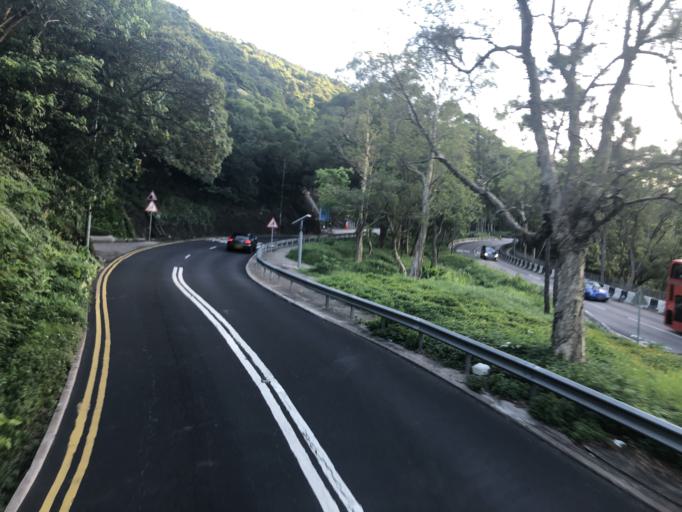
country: HK
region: Sai Kung
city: Sai Kung
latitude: 22.3438
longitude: 114.2525
